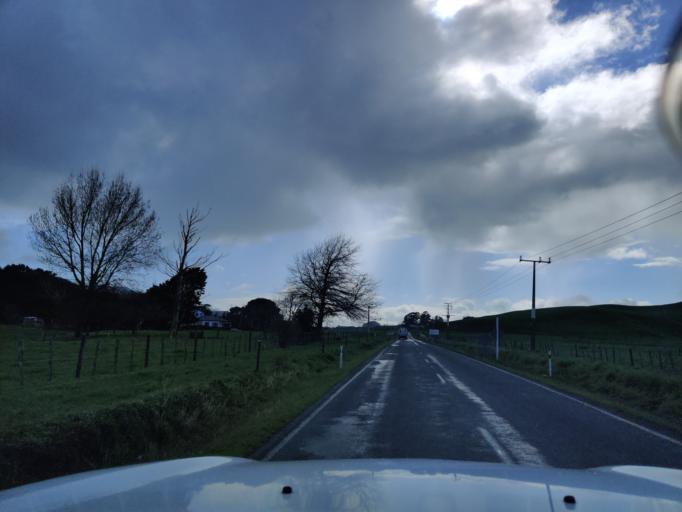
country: NZ
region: Waikato
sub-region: Waikato District
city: Ngaruawahia
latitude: -37.5933
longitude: 175.2083
